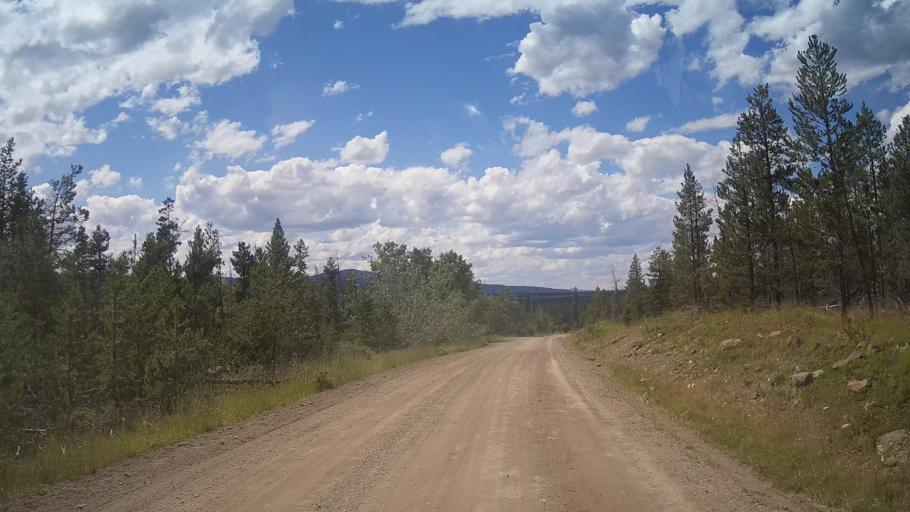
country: CA
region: British Columbia
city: Lillooet
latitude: 51.3394
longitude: -121.9469
